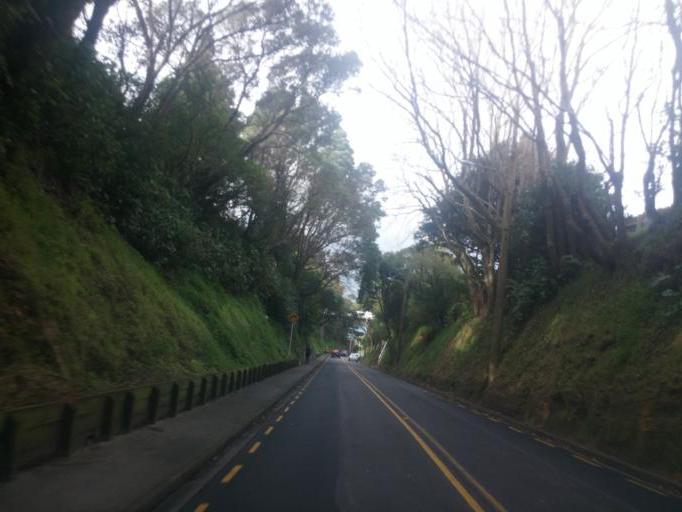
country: NZ
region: Wellington
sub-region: Wellington City
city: Wellington
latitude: -41.2642
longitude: 174.7793
